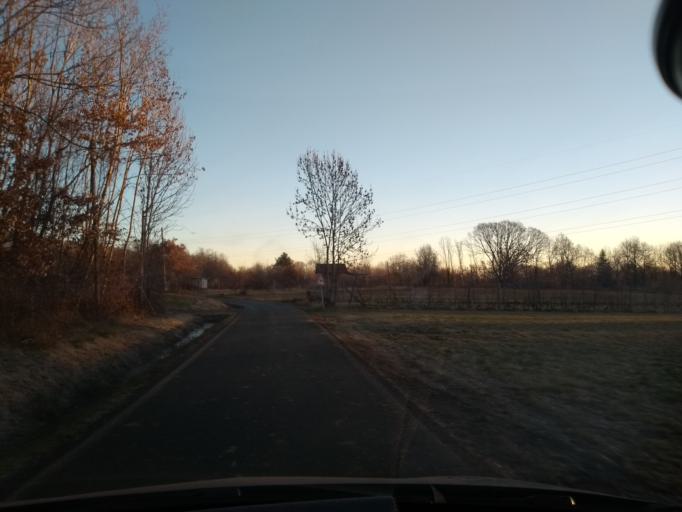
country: IT
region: Piedmont
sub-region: Provincia di Torino
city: Balangero
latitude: 45.2748
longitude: 7.5337
